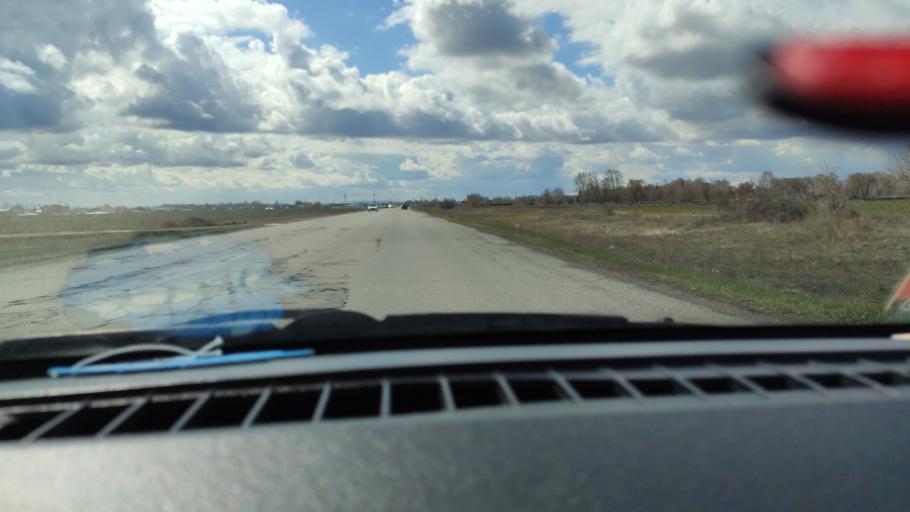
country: RU
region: Samara
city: Tol'yatti
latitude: 53.6824
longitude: 49.4162
